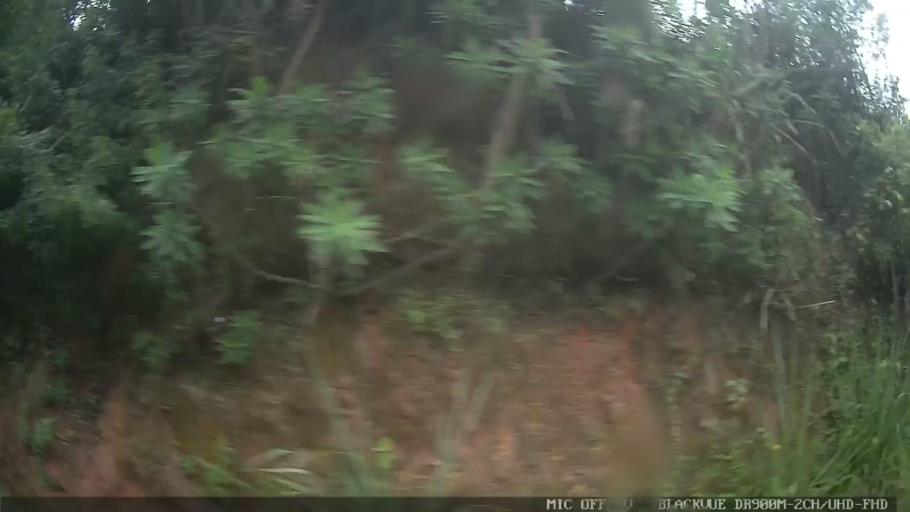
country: BR
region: Sao Paulo
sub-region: Atibaia
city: Atibaia
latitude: -23.1582
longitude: -46.5989
